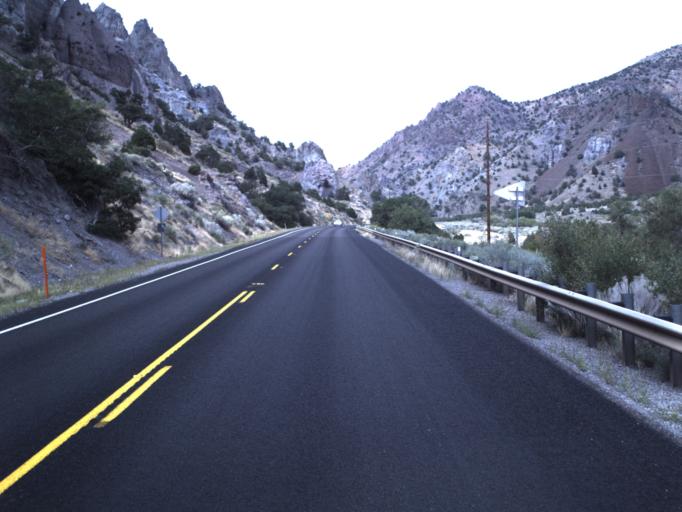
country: US
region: Utah
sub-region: Sevier County
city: Monroe
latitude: 38.5437
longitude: -112.2692
